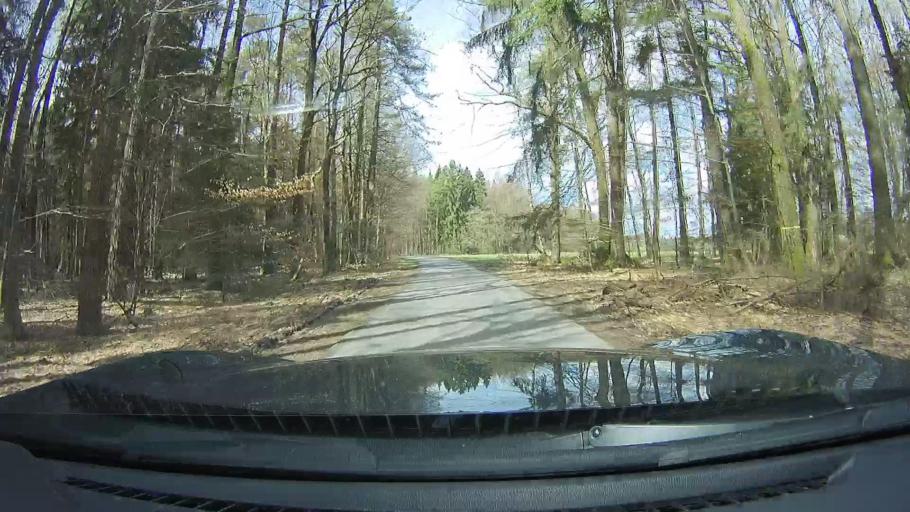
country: DE
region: Hesse
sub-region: Regierungsbezirk Darmstadt
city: Hesseneck
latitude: 49.5837
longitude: 9.0908
